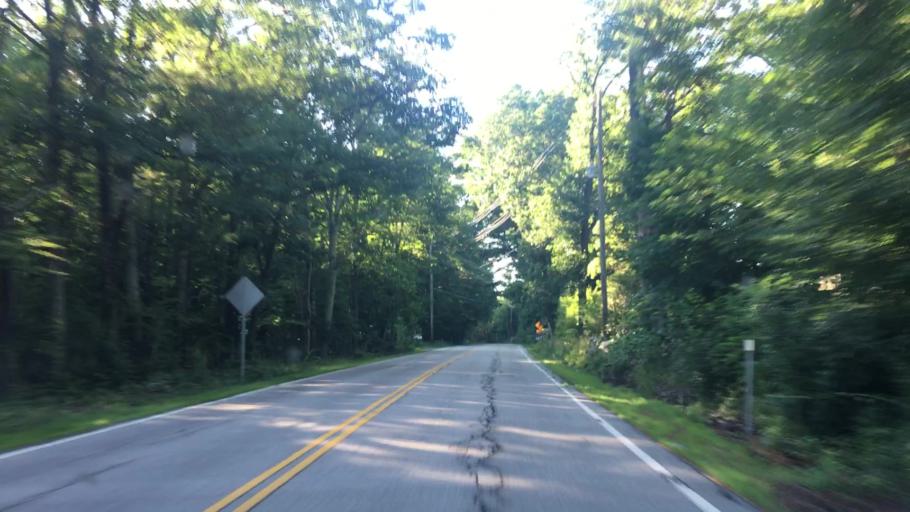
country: US
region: New Hampshire
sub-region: Rockingham County
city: Sandown
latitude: 42.9525
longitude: -71.1963
